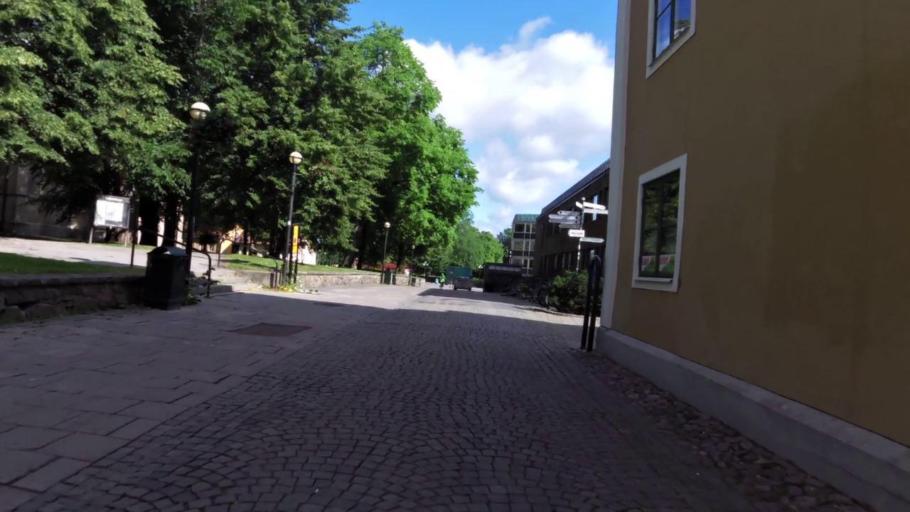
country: SE
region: OEstergoetland
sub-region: Linkopings Kommun
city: Linkoping
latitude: 58.4109
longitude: 15.6195
